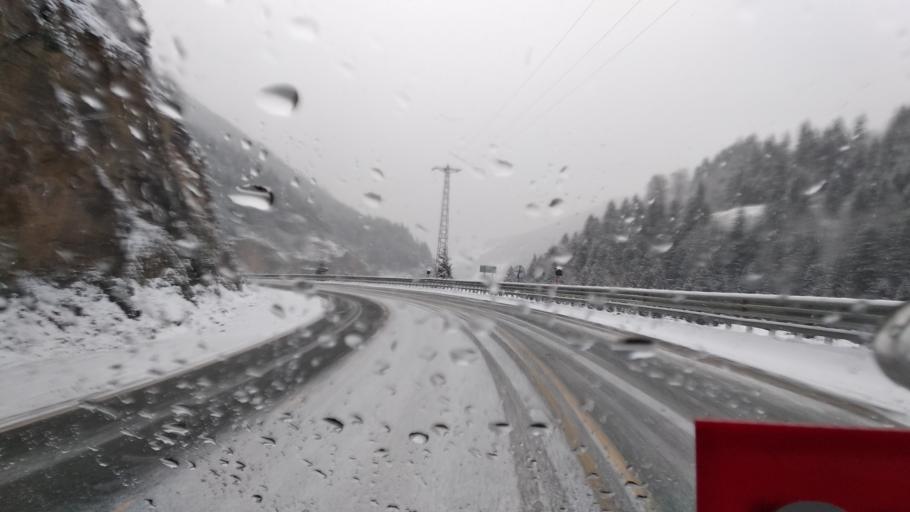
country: TR
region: Gumushane
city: Yaglidere
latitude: 40.6758
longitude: 39.4378
